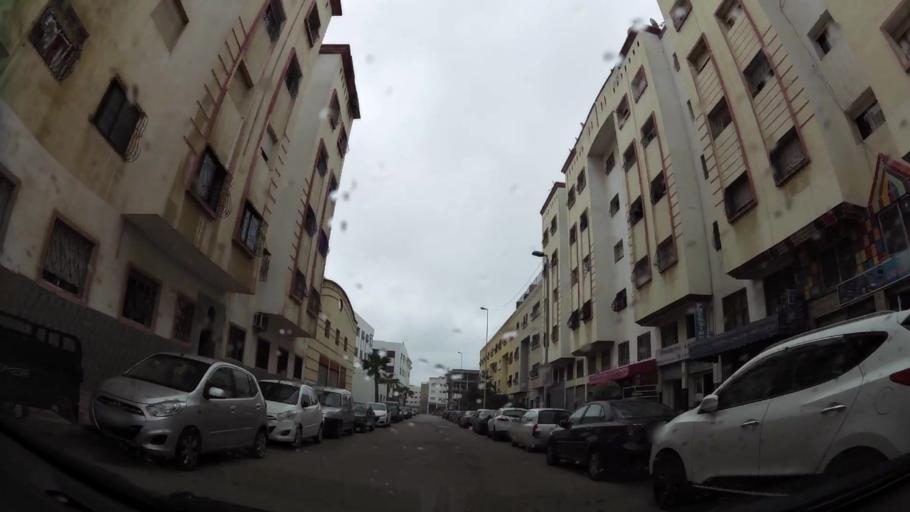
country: MA
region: Grand Casablanca
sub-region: Casablanca
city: Casablanca
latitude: 33.5361
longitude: -7.6098
